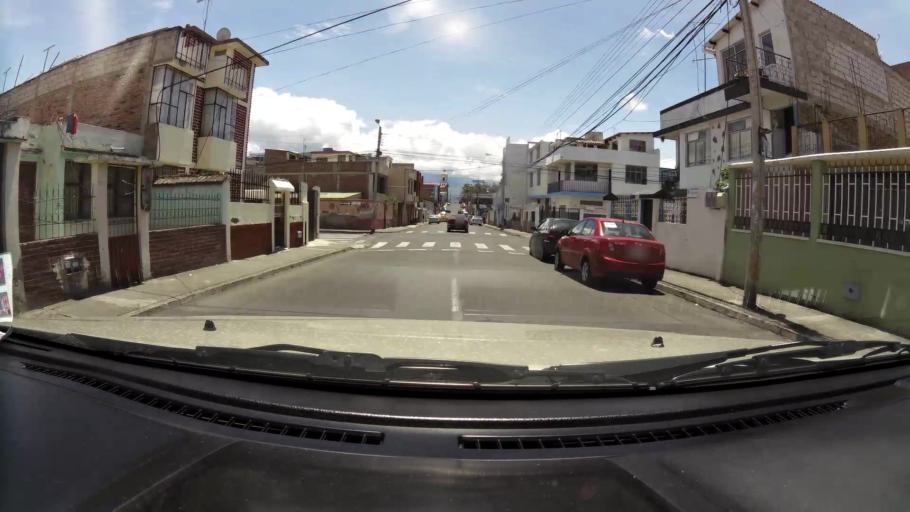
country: EC
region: Chimborazo
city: Riobamba
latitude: -1.6641
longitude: -78.6552
